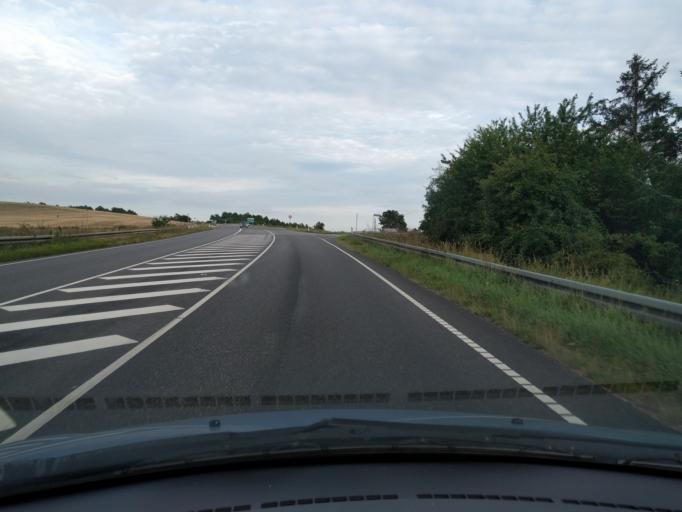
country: DK
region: Zealand
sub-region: Vordingborg Kommune
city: Nyrad
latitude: 55.0019
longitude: 11.9858
